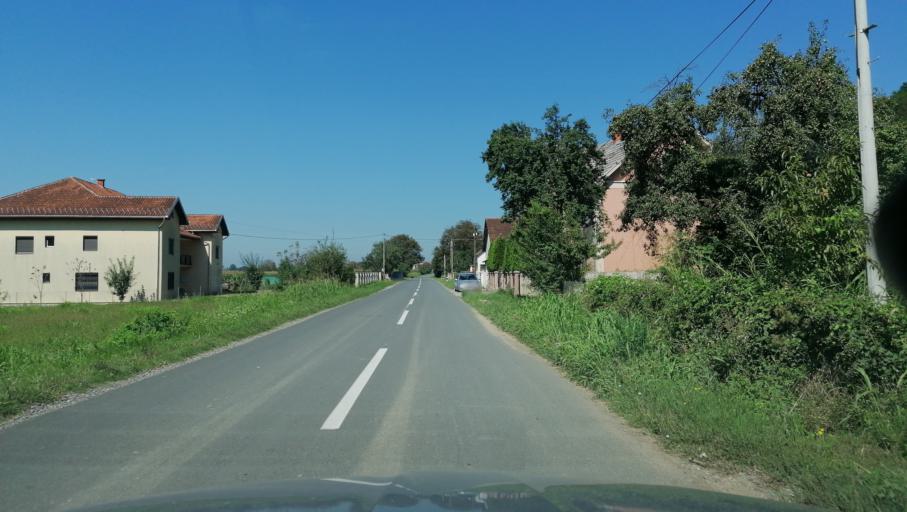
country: RS
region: Central Serbia
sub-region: Raski Okrug
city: Vrnjacka Banja
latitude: 43.6641
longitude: 20.9200
